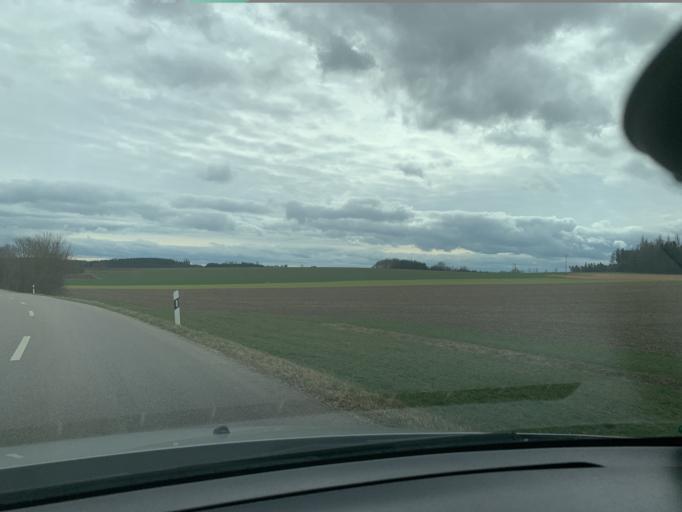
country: DE
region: Bavaria
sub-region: Lower Bavaria
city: Kumhausen
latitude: 48.5018
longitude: 12.2028
